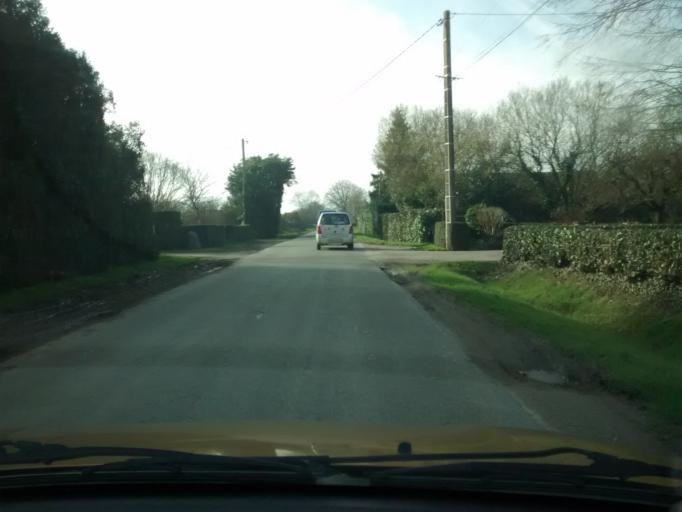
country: FR
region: Pays de la Loire
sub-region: Departement de la Loire-Atlantique
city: Notre-Dame-des-Landes
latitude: 47.3573
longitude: -1.7291
